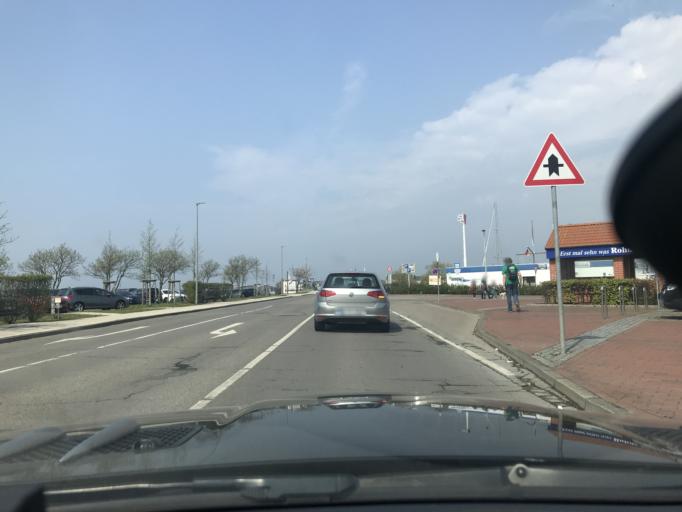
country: DE
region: Schleswig-Holstein
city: Heiligenhafen
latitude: 54.3744
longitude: 10.9806
